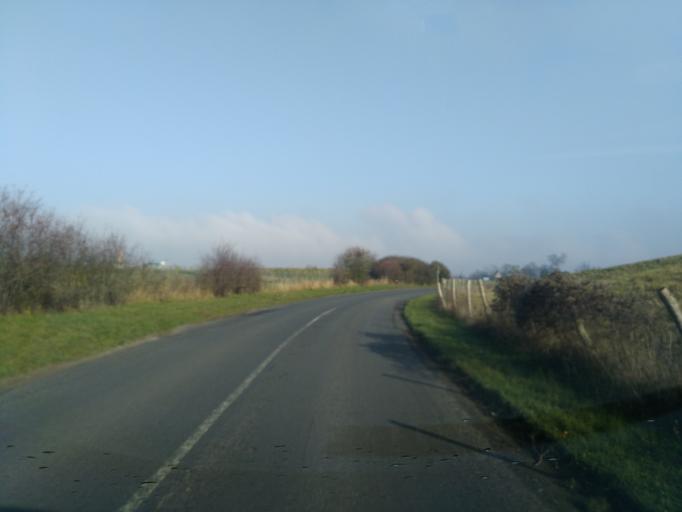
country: FR
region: Ile-de-France
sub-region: Departement des Yvelines
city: Thiverval-Grignon
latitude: 48.8415
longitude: 1.9146
